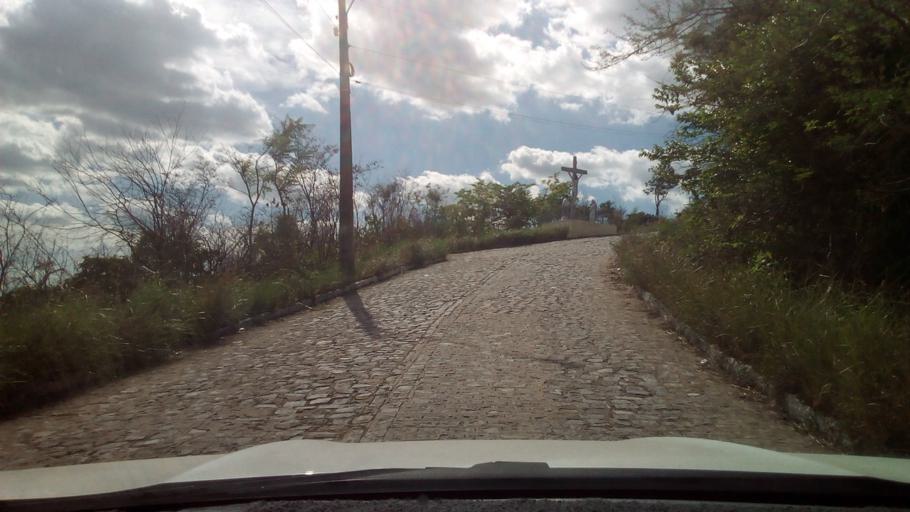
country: BR
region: Paraiba
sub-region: Guarabira
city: Guarabira
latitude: -6.8330
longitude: -35.4963
